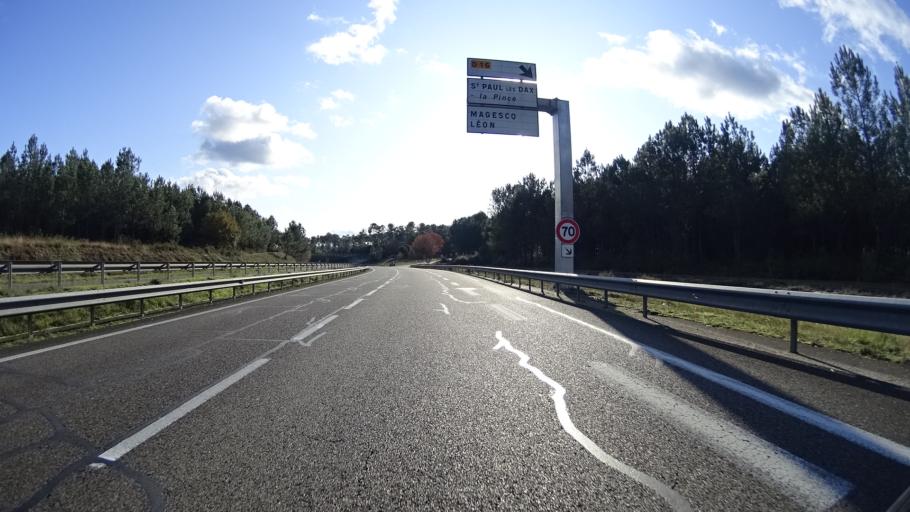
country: FR
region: Aquitaine
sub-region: Departement des Landes
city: Mees
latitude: 43.7350
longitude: -1.1017
